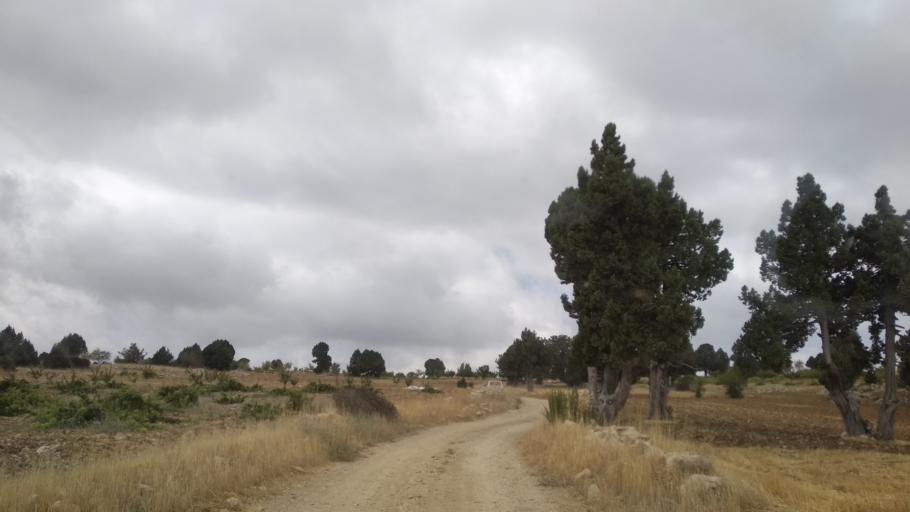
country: TR
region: Mersin
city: Sarikavak
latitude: 36.5649
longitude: 33.7688
